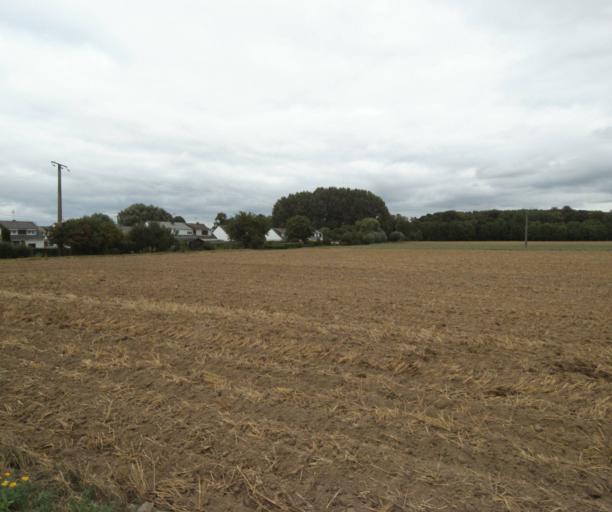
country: FR
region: Nord-Pas-de-Calais
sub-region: Departement du Nord
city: Ennevelin
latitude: 50.5521
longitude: 3.1262
